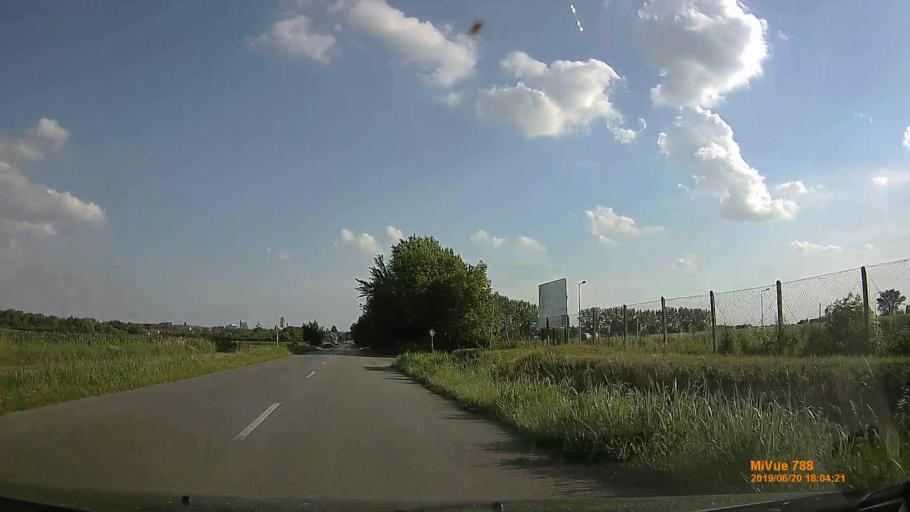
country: HU
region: Baranya
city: Szentlorinc
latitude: 46.0516
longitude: 17.9884
